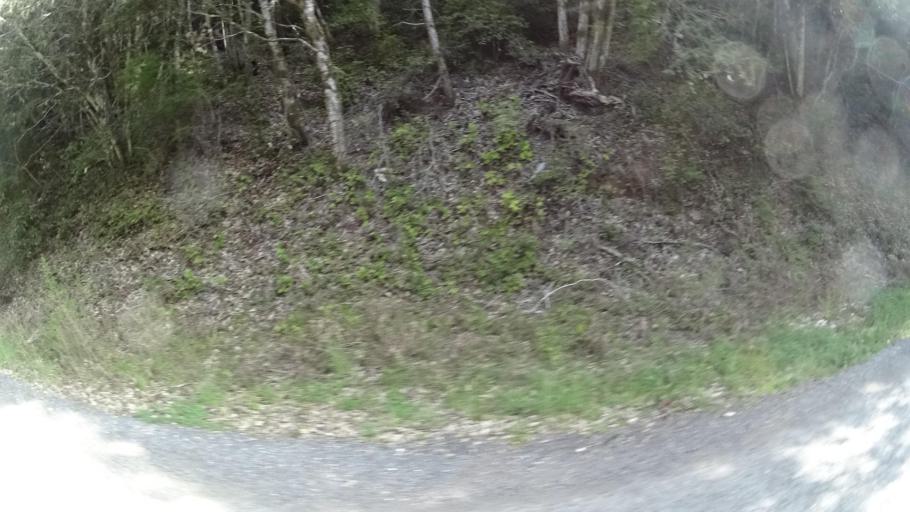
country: US
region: California
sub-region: Humboldt County
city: Blue Lake
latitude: 40.6975
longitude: -123.9388
